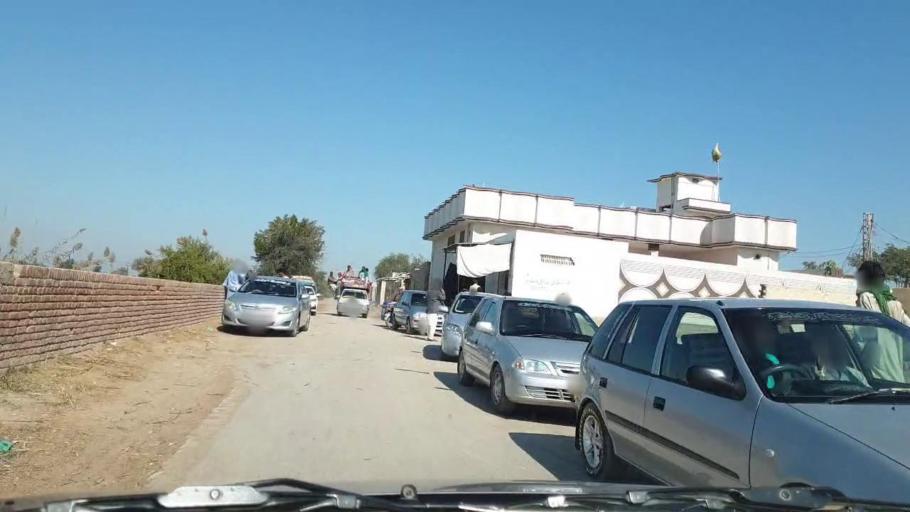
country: PK
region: Sindh
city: Sinjhoro
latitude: 26.1229
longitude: 68.8191
